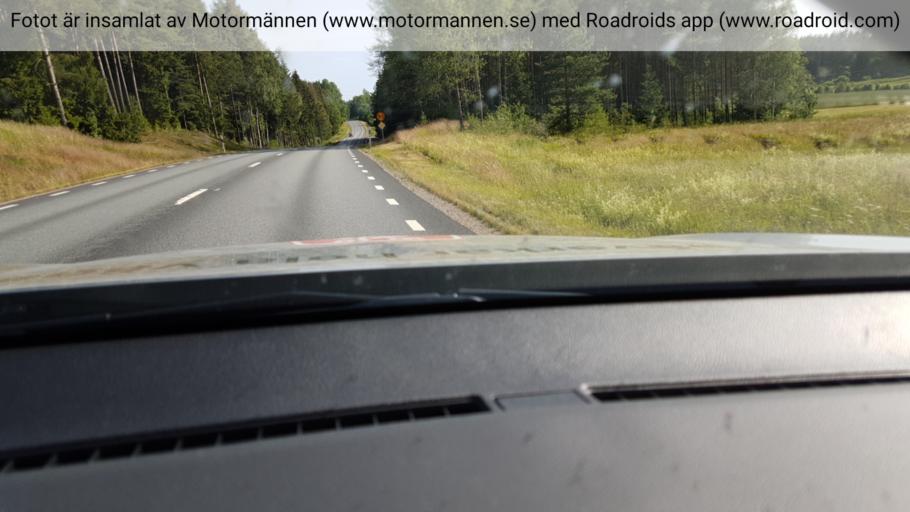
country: SE
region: Joenkoeping
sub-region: Vetlanda Kommun
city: Ekenassjon
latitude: 57.5324
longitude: 14.9912
